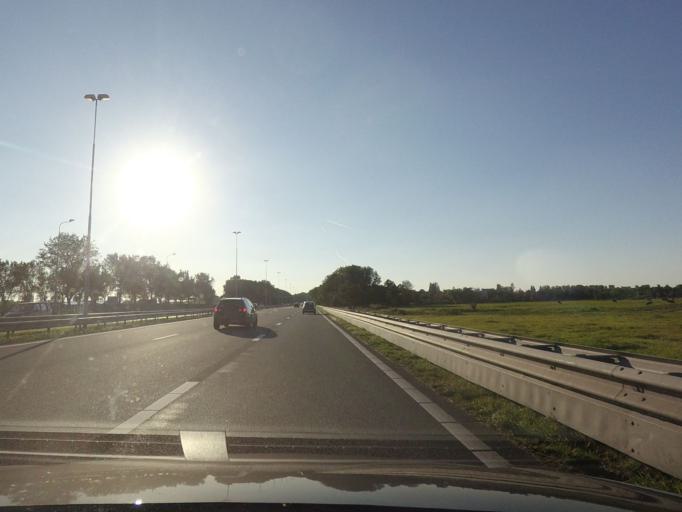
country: NL
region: North Holland
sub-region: Gemeente Haarlem
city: Haarlem
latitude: 52.3712
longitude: 4.6887
